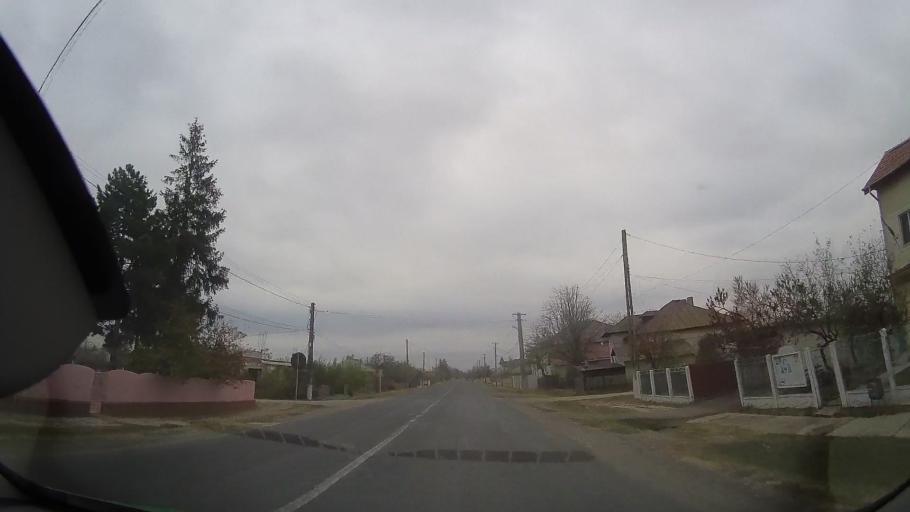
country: RO
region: Buzau
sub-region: Comuna Padina
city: Padina
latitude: 44.8280
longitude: 27.1125
